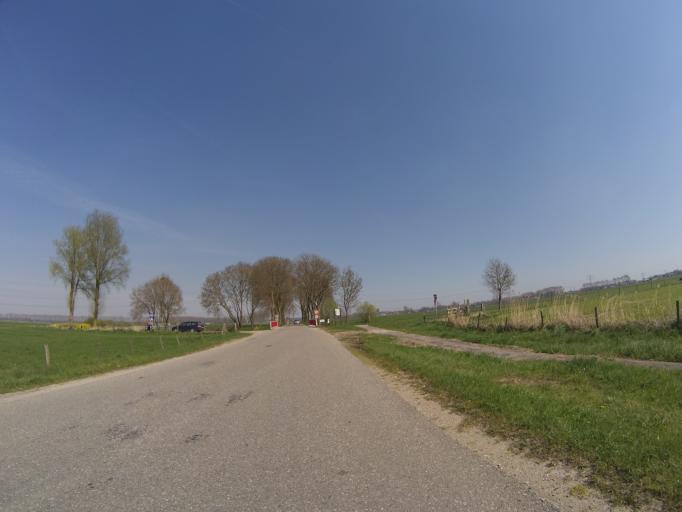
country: NL
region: Gelderland
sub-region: Gemeente Wageningen
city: Wageningen
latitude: 51.9661
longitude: 5.6174
